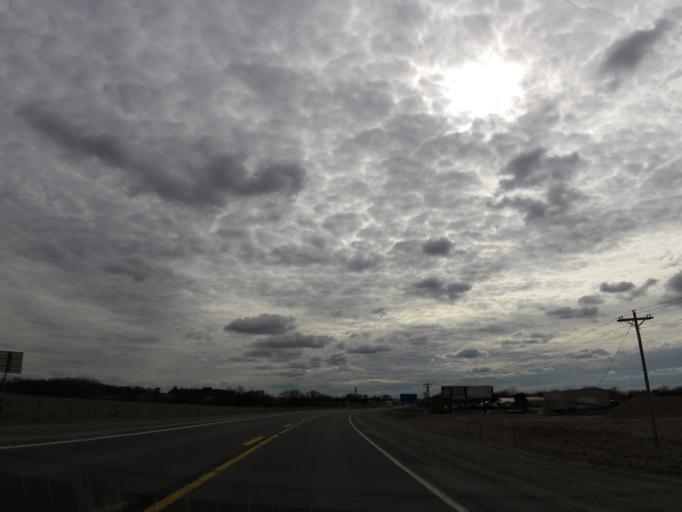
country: US
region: Iowa
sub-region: Chickasaw County
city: New Hampton
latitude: 43.0898
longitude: -92.3007
